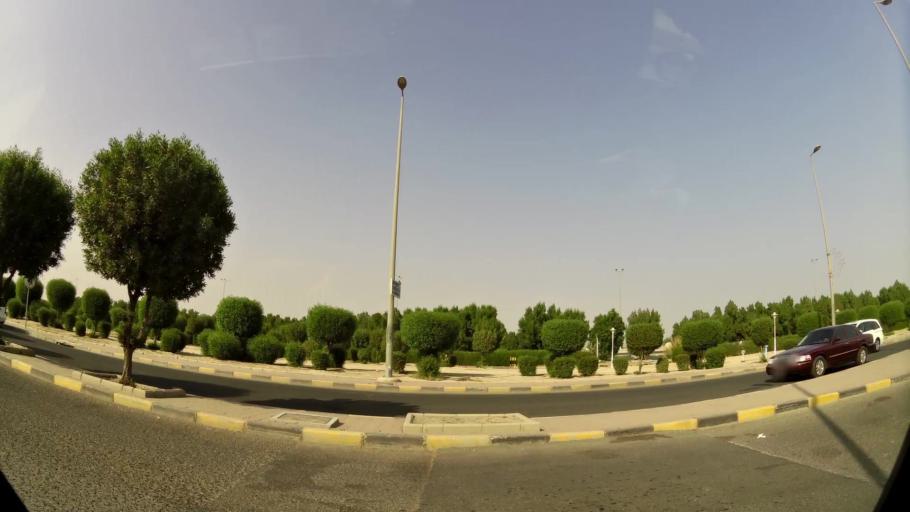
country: KW
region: Muhafazat al Jahra'
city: Al Jahra'
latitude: 29.3476
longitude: 47.6959
